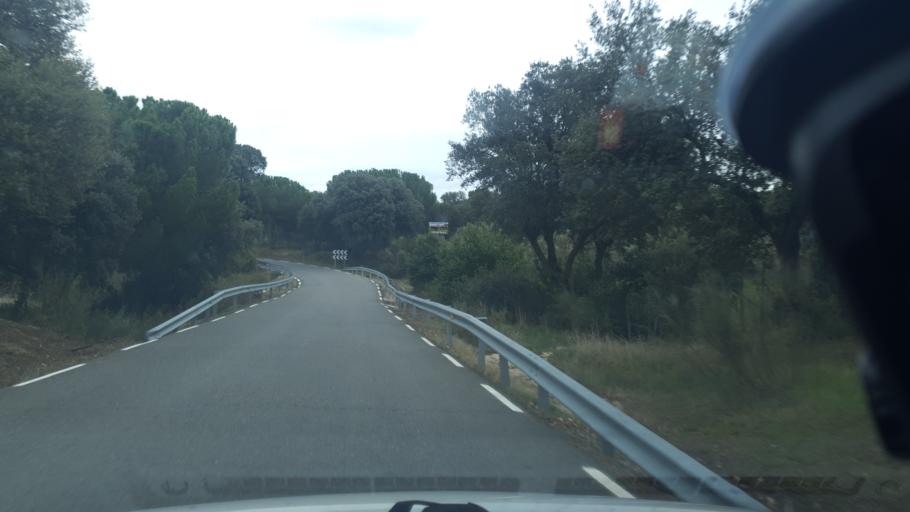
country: ES
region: Castille and Leon
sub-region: Provincia de Avila
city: Gotarrendura
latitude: 40.8254
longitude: -4.7038
